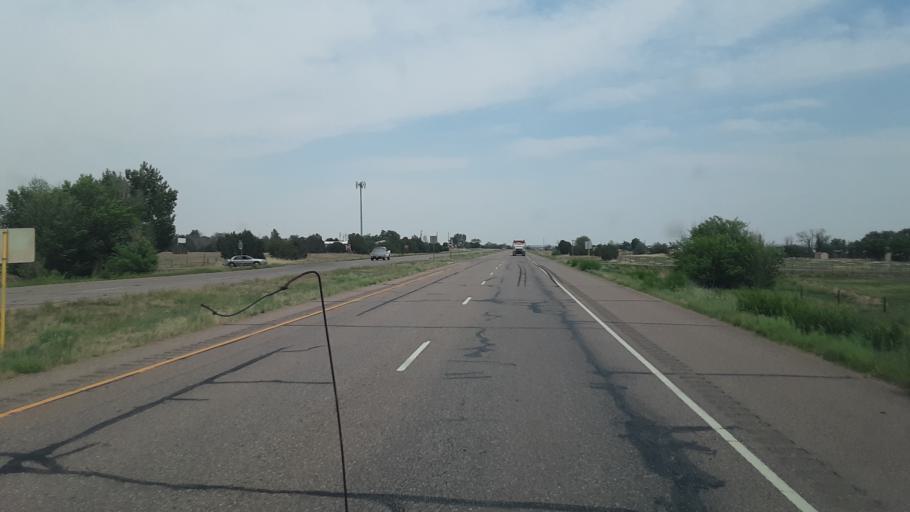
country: US
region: Colorado
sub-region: Fremont County
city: Penrose
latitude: 38.4057
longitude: -104.9930
